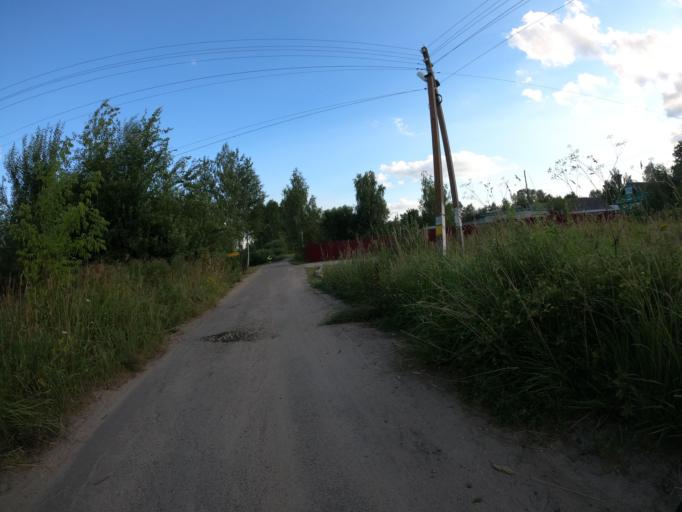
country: RU
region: Moskovskaya
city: Ashitkovo
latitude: 55.4237
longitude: 38.5821
